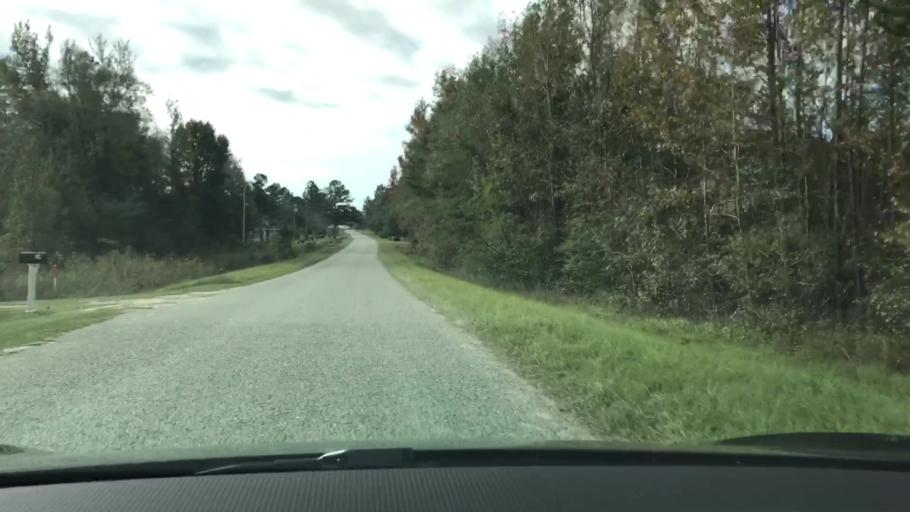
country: US
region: Georgia
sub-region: Jefferson County
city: Wadley
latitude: 32.8047
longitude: -82.3453
